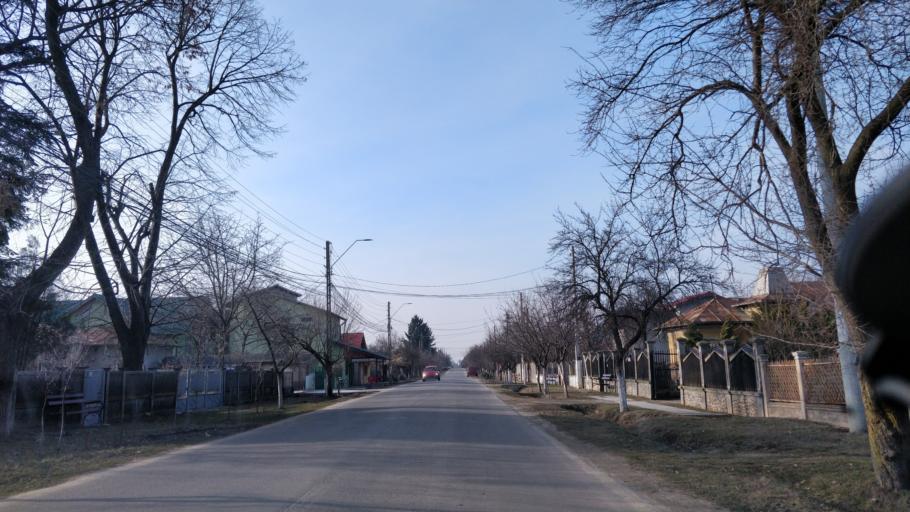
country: RO
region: Giurgiu
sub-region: Comuna Ulmi
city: Trestieni
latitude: 44.4981
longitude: 25.7691
